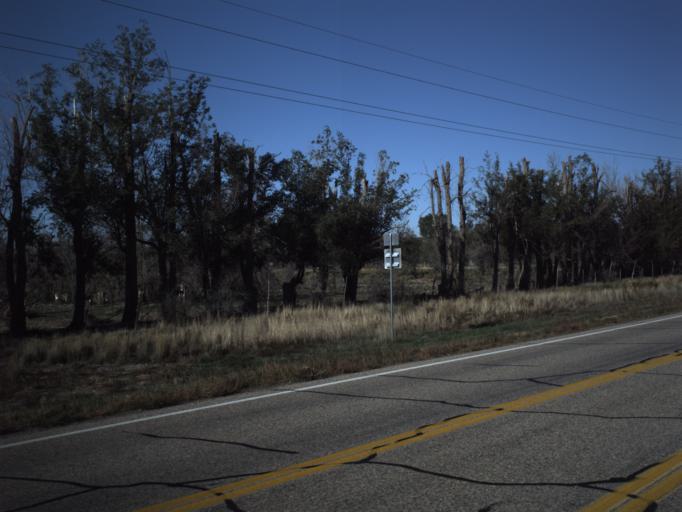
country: US
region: Utah
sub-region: Washington County
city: Enterprise
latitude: 37.7102
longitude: -113.6583
